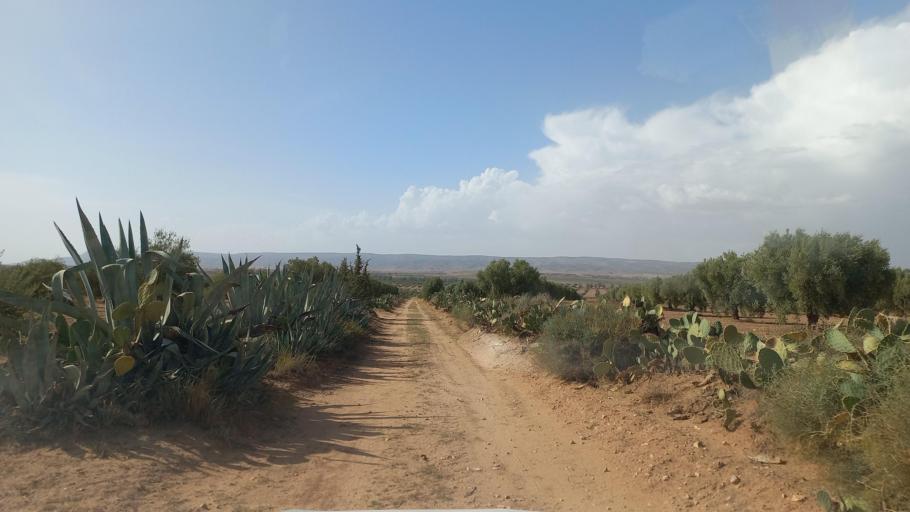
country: TN
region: Al Qasrayn
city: Kasserine
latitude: 35.2117
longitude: 8.9534
